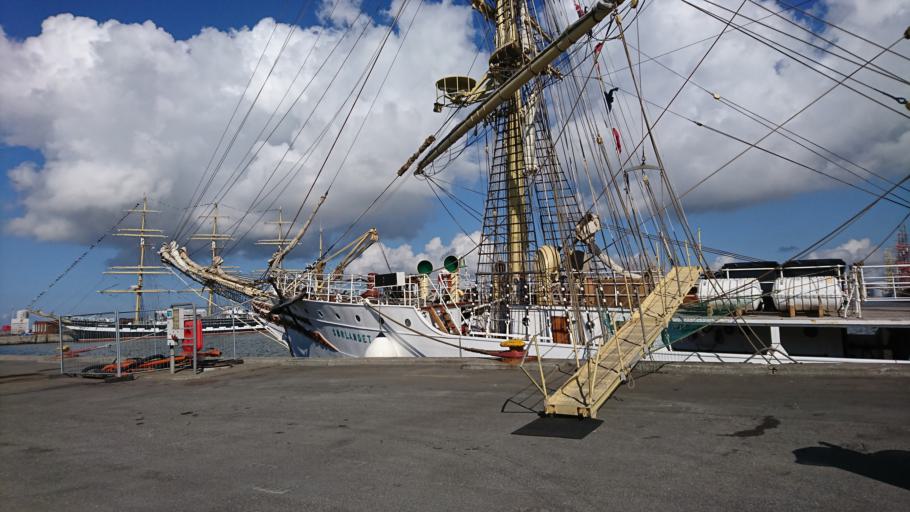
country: DK
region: South Denmark
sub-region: Esbjerg Kommune
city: Esbjerg
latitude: 55.4660
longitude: 8.4359
